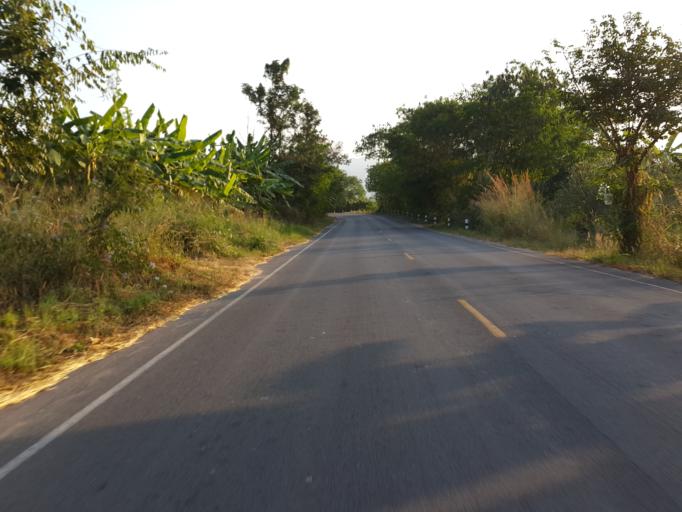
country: TH
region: Lamphun
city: Thung Hua Chang
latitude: 17.8888
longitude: 99.0609
